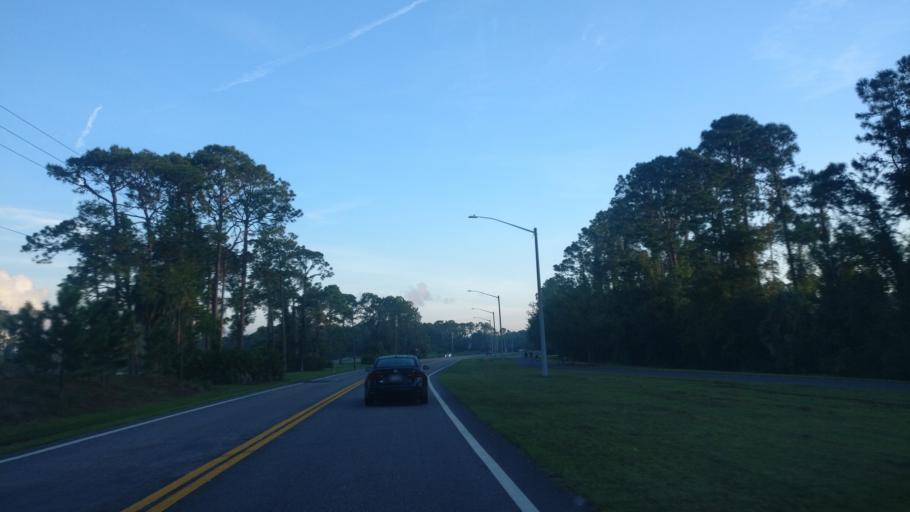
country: US
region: Florida
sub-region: Flagler County
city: Palm Coast
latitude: 29.5388
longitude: -81.2384
